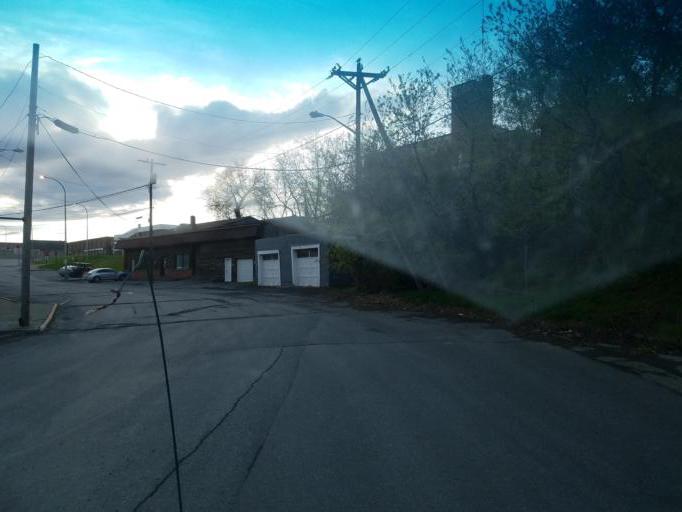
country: US
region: Maine
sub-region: Aroostook County
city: Caribou
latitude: 46.8598
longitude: -68.0103
